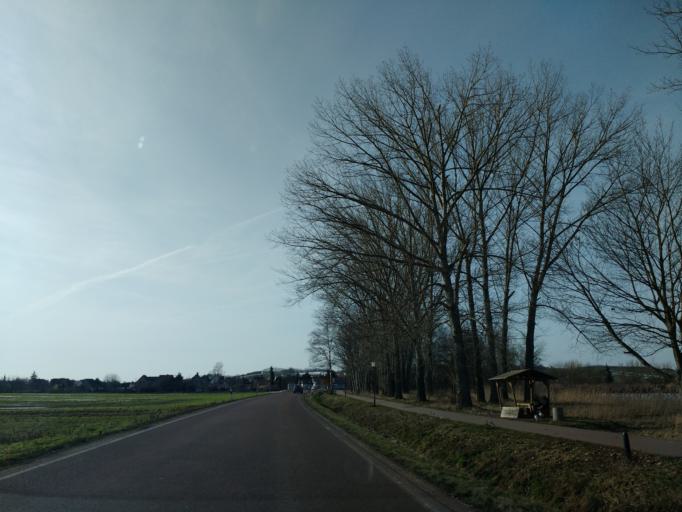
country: DE
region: Saxony-Anhalt
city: Sennewitz
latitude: 51.5461
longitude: 11.9614
